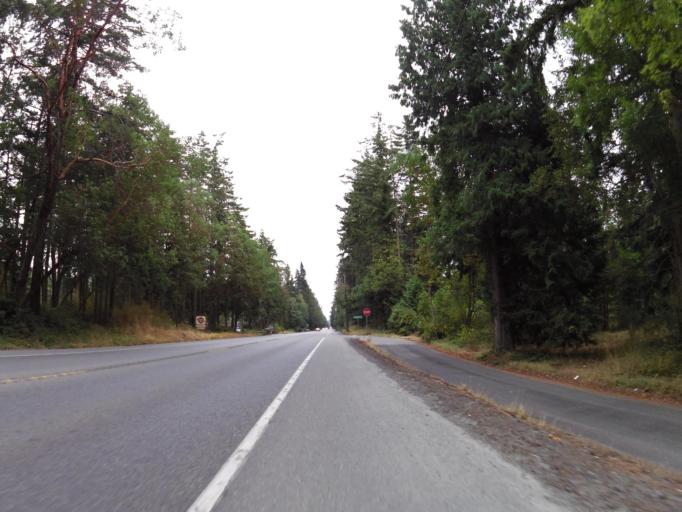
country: US
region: Washington
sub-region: Jefferson County
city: Port Hadlock-Irondale
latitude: 48.0656
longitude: -122.8130
